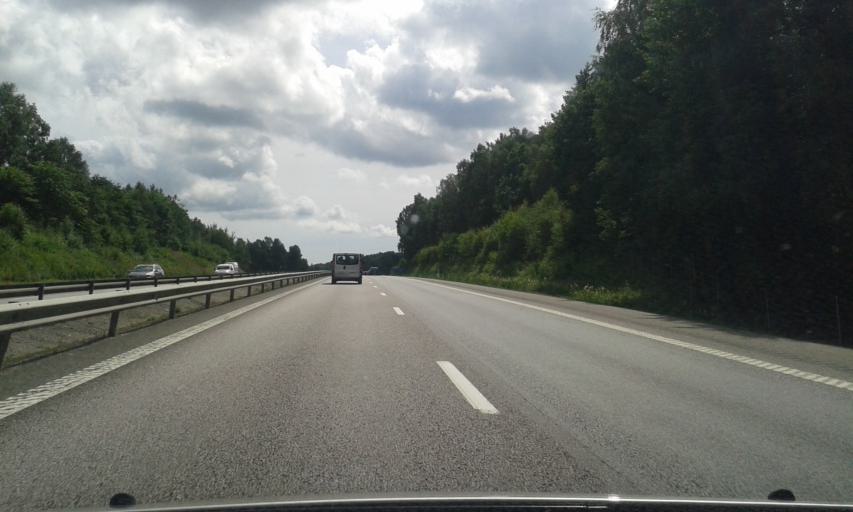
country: SE
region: Halland
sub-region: Kungsbacka Kommun
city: Kungsbacka
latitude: 57.4942
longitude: 12.0491
